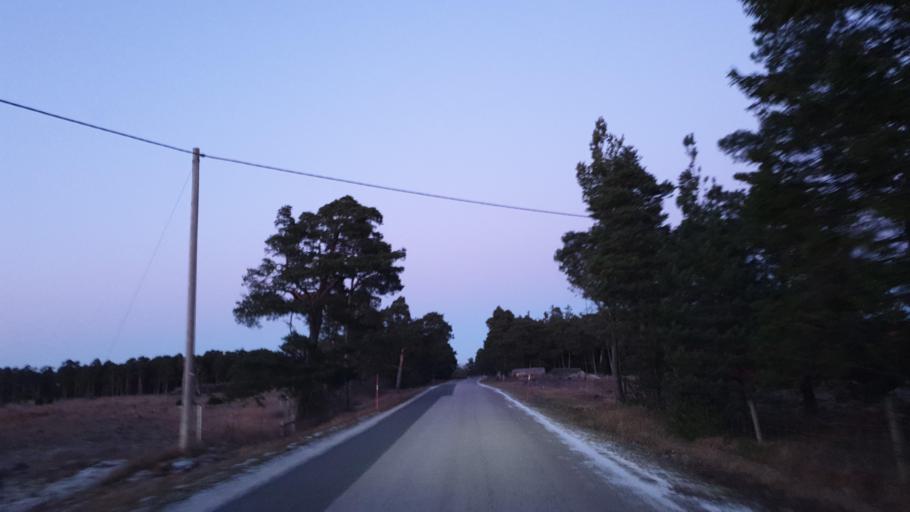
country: SE
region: Gotland
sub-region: Gotland
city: Slite
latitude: 57.4134
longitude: 18.8118
